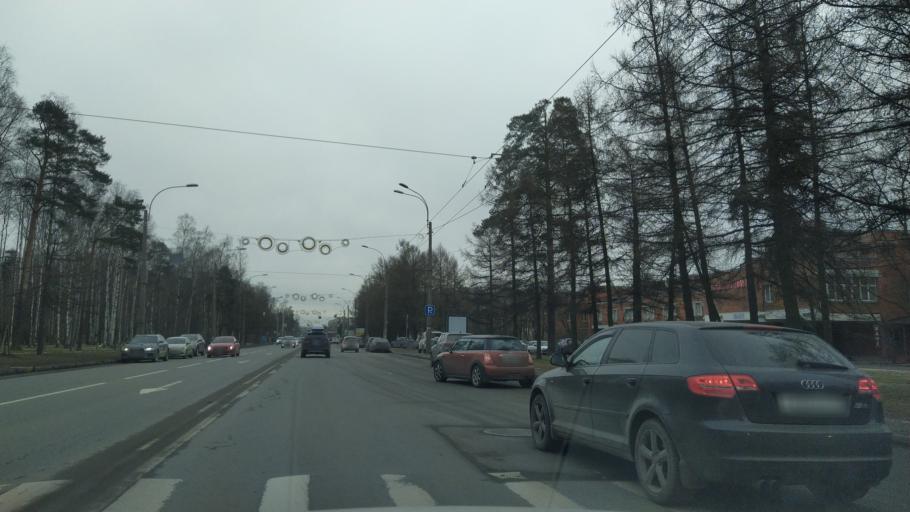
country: RU
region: St.-Petersburg
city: Sosnovka
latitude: 60.0149
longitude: 30.3406
